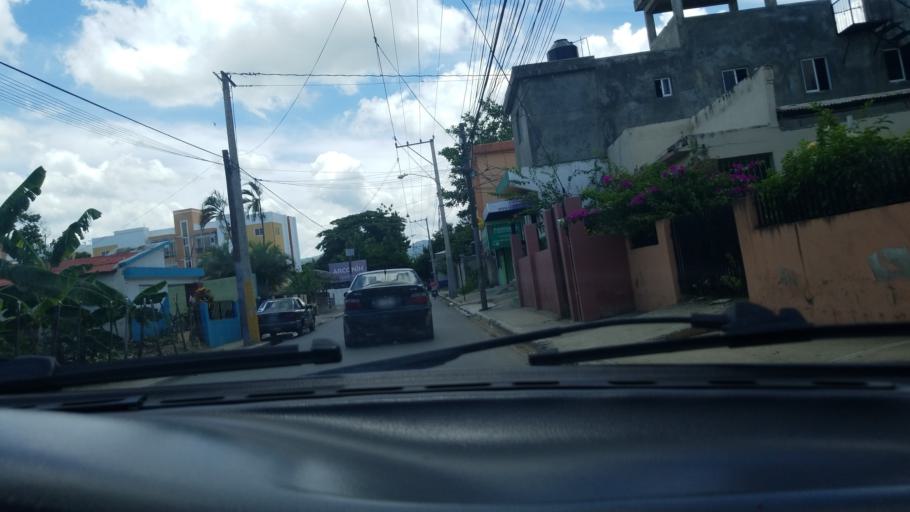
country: DO
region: Santiago
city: Santiago de los Caballeros
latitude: 19.4811
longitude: -70.6807
